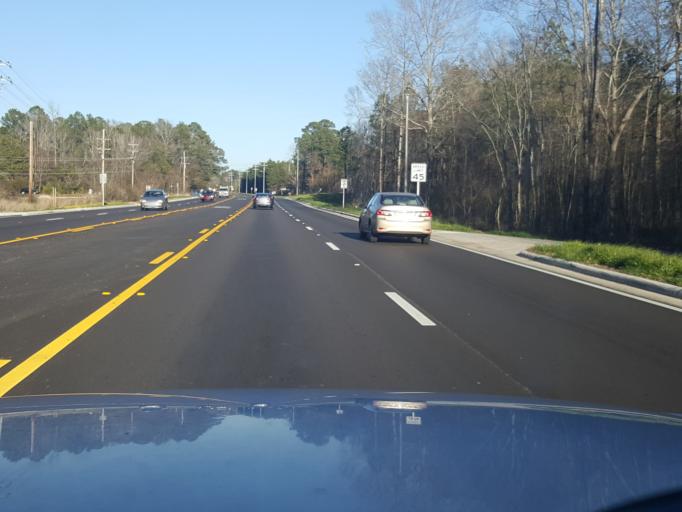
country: US
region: Mississippi
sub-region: Rankin County
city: Flowood
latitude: 32.3269
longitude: -90.0985
